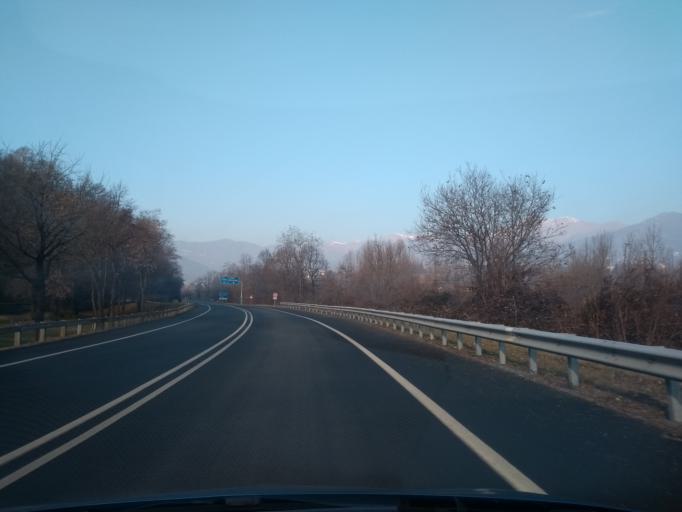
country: IT
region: Piedmont
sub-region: Provincia di Torino
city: Lanzo Torinese
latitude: 45.2655
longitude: 7.4980
